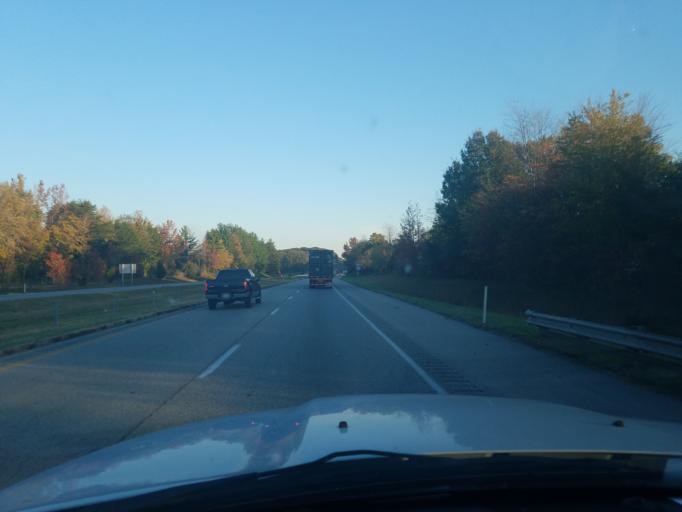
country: US
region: Indiana
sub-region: Clark County
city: Henryville
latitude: 38.5463
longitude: -85.7784
